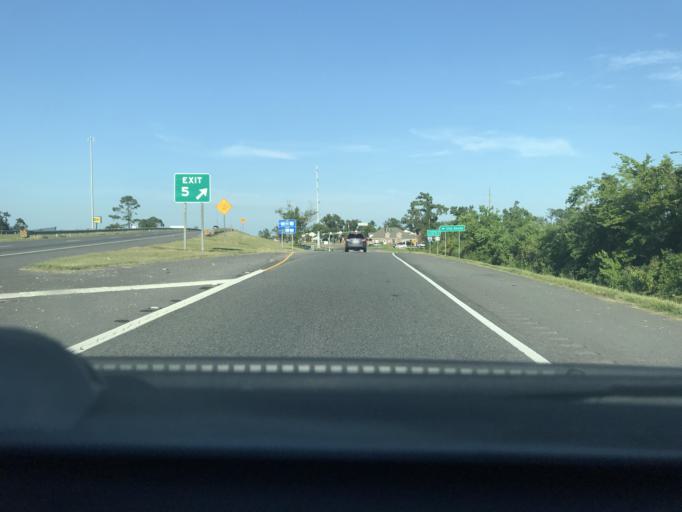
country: US
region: Louisiana
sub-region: Calcasieu Parish
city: Lake Charles
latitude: 30.1968
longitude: -93.2345
